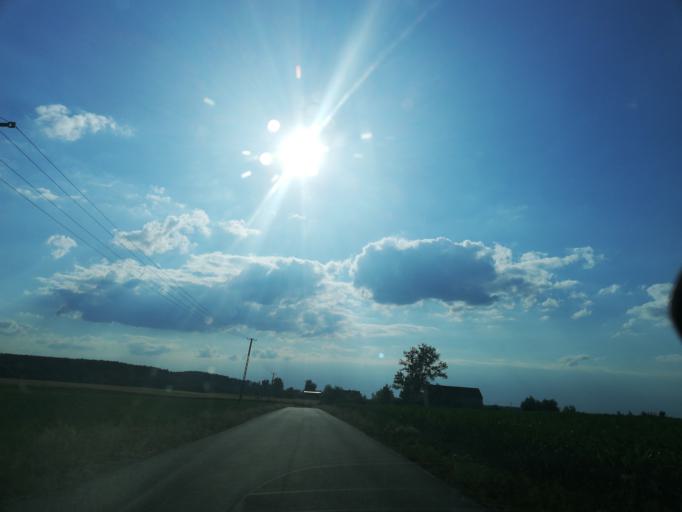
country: PL
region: Kujawsko-Pomorskie
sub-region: Powiat golubsko-dobrzynski
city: Golub-Dobrzyn
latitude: 53.0288
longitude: 19.0411
